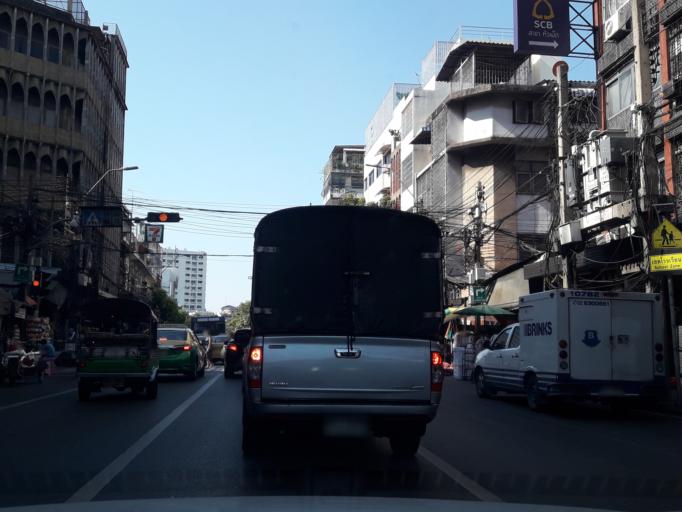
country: TH
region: Bangkok
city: Bangkok
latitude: 13.7435
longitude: 100.5040
